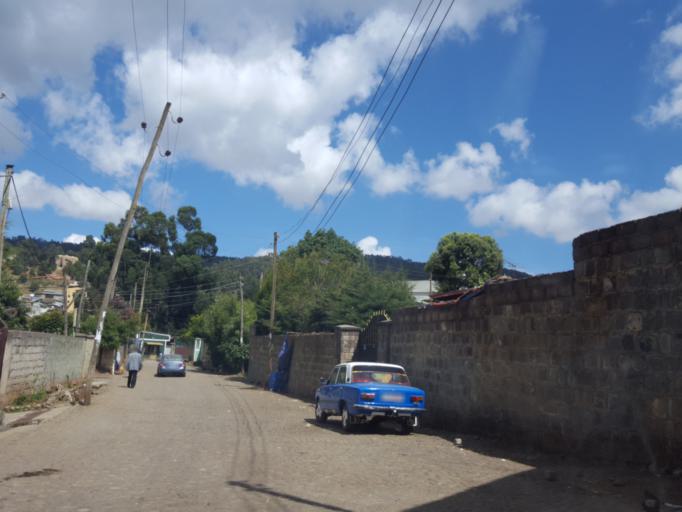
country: ET
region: Adis Abeba
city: Addis Ababa
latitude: 9.0684
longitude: 38.7347
